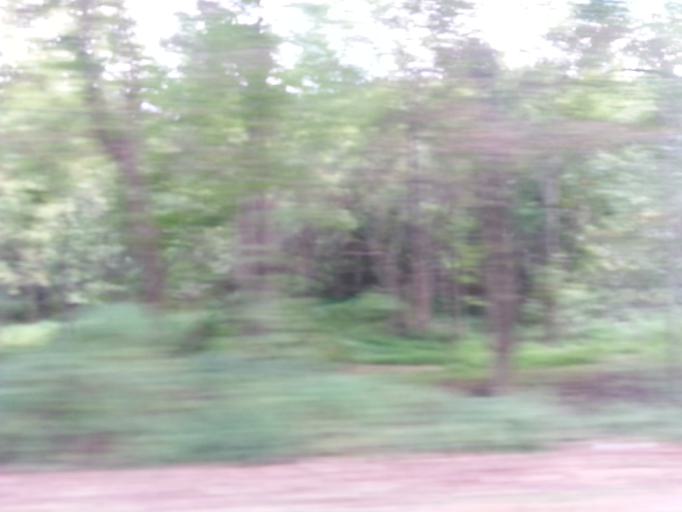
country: US
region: Tennessee
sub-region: Knox County
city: Mascot
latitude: 36.0978
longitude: -83.7718
